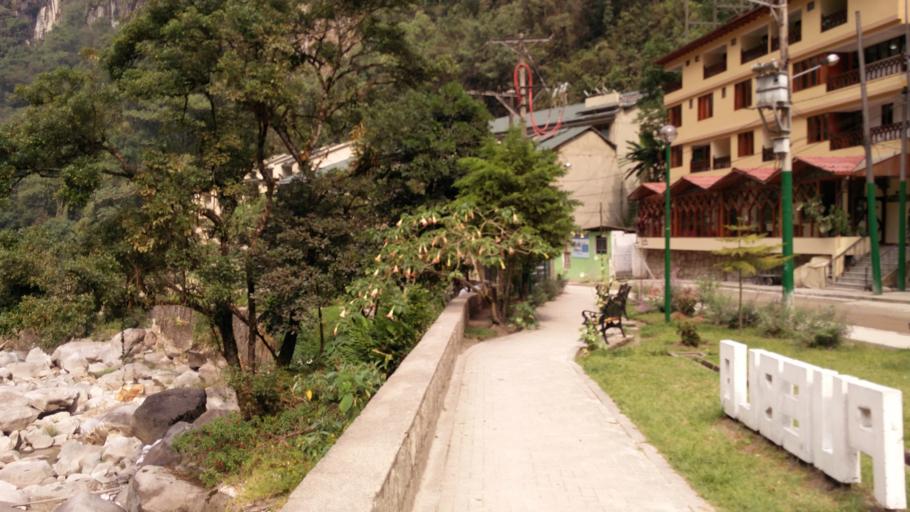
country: PE
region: Cusco
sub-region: Provincia de La Convencion
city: Santa Teresa
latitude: -13.1543
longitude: -72.5275
